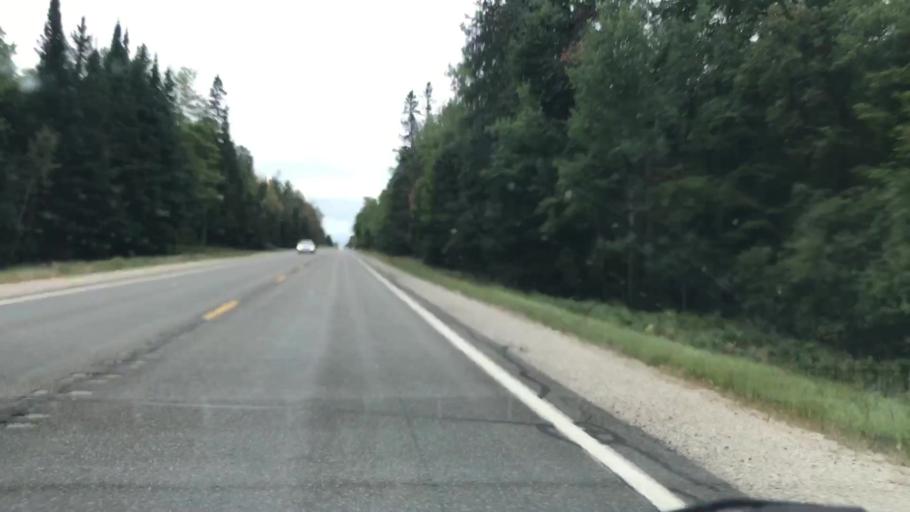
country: US
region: Michigan
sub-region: Luce County
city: Newberry
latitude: 46.2261
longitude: -85.5721
